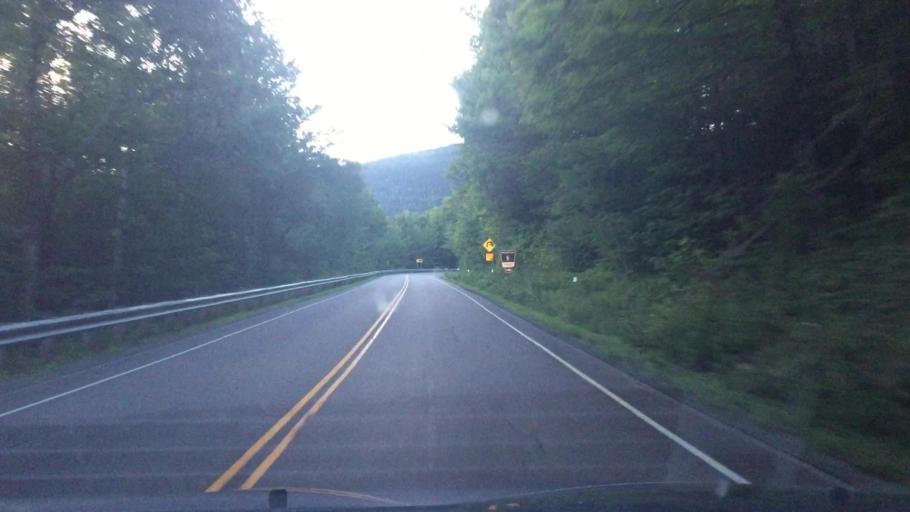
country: US
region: New Hampshire
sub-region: Grafton County
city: Woodstock
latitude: 44.0397
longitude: -71.5234
